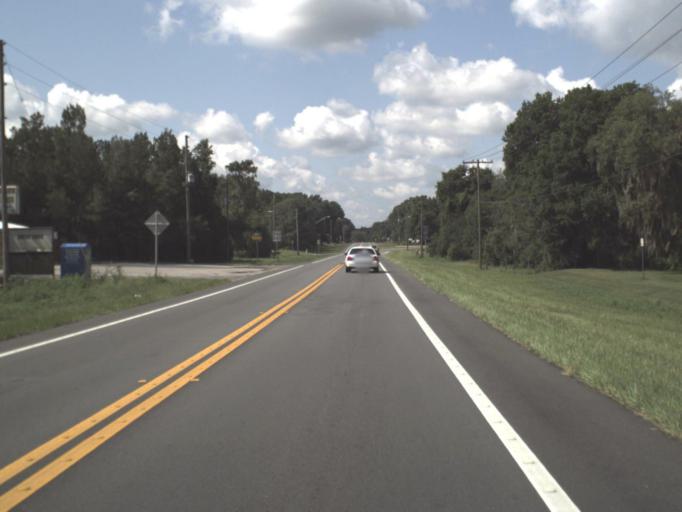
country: US
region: Florida
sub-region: Citrus County
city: Floral City
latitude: 28.7344
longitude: -82.3028
